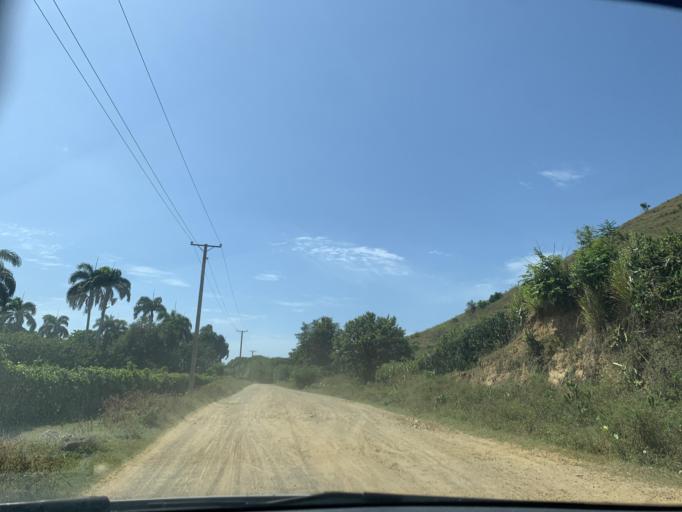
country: DO
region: Puerto Plata
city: Luperon
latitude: 19.8843
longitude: -70.8725
